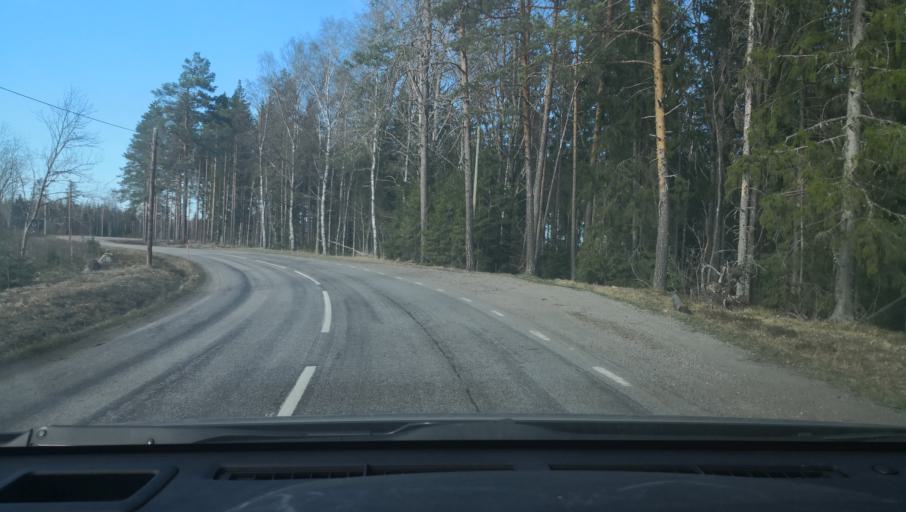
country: SE
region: Uppsala
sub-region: Heby Kommun
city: Morgongava
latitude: 59.9858
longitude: 16.9125
